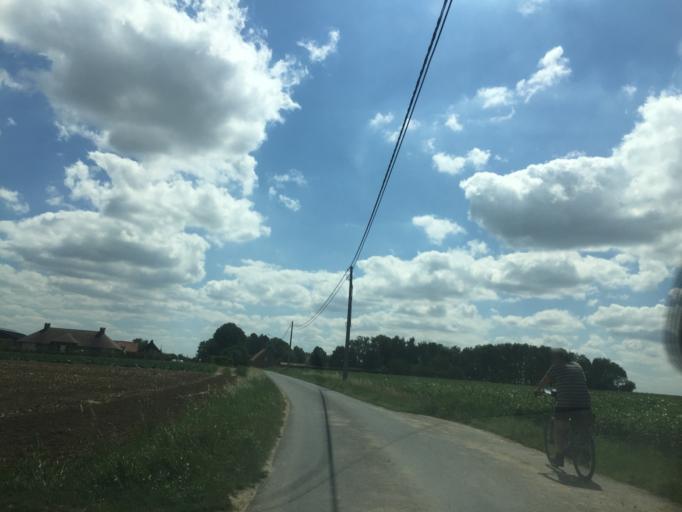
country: BE
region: Flanders
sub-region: Provincie West-Vlaanderen
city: Staden
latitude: 50.9705
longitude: 2.9936
